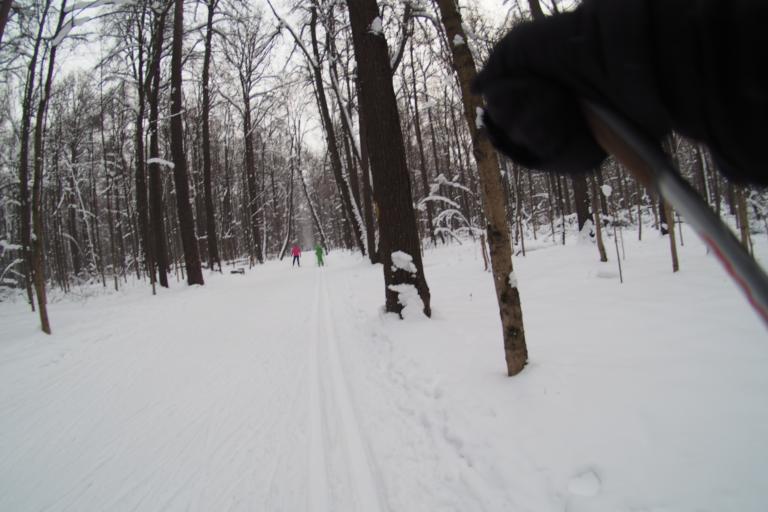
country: RU
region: Moskovskaya
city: Izmaylovo
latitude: 55.7713
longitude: 37.7772
